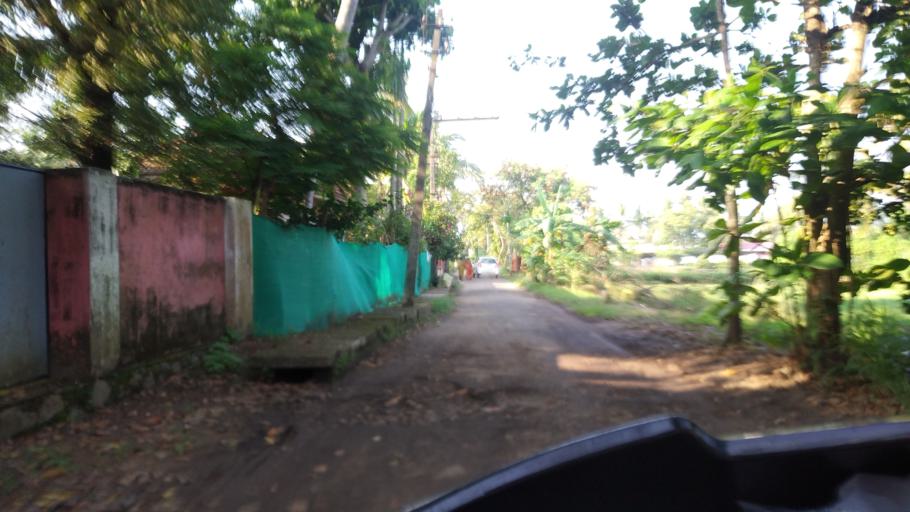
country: IN
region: Kerala
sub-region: Ernakulam
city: Elur
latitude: 10.0438
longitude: 76.2270
